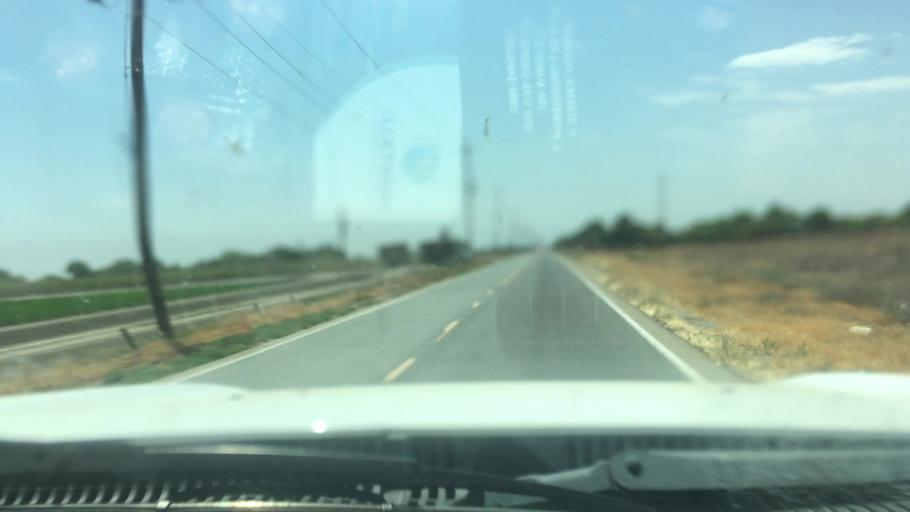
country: US
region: California
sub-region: Kings County
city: Corcoran
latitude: 36.0508
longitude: -119.4988
